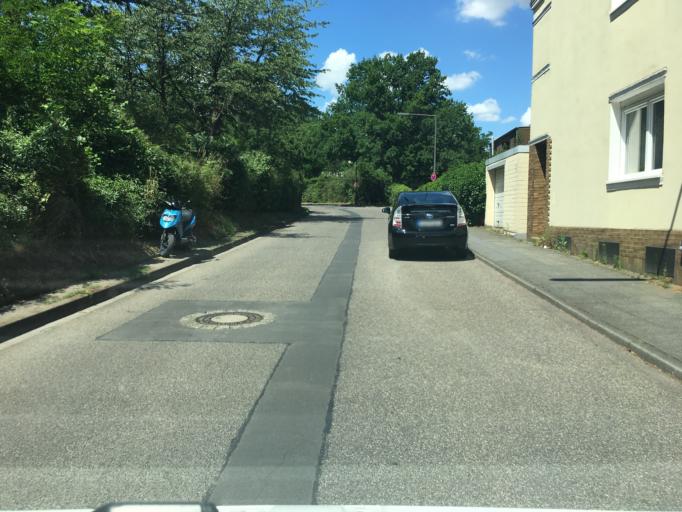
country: DE
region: North Rhine-Westphalia
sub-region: Regierungsbezirk Koln
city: Mengenich
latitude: 50.9786
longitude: 6.8597
